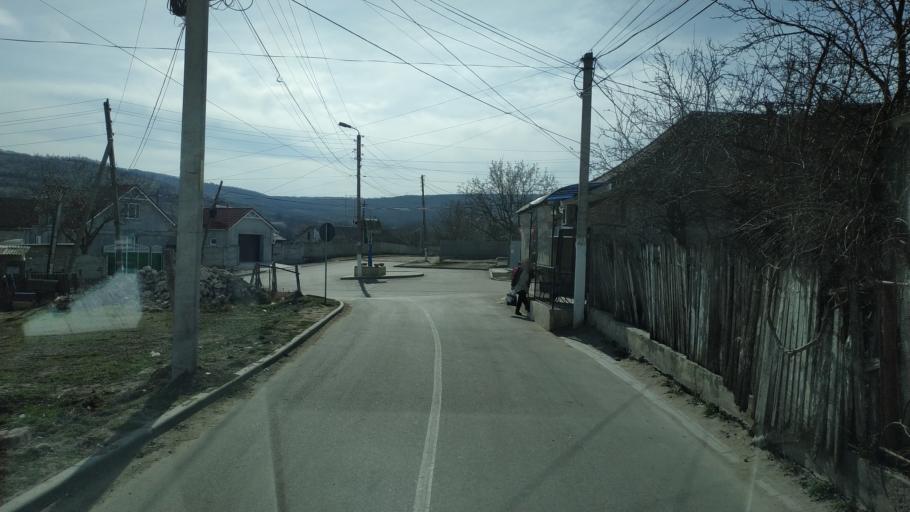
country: MD
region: Straseni
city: Straseni
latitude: 47.0943
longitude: 28.6511
